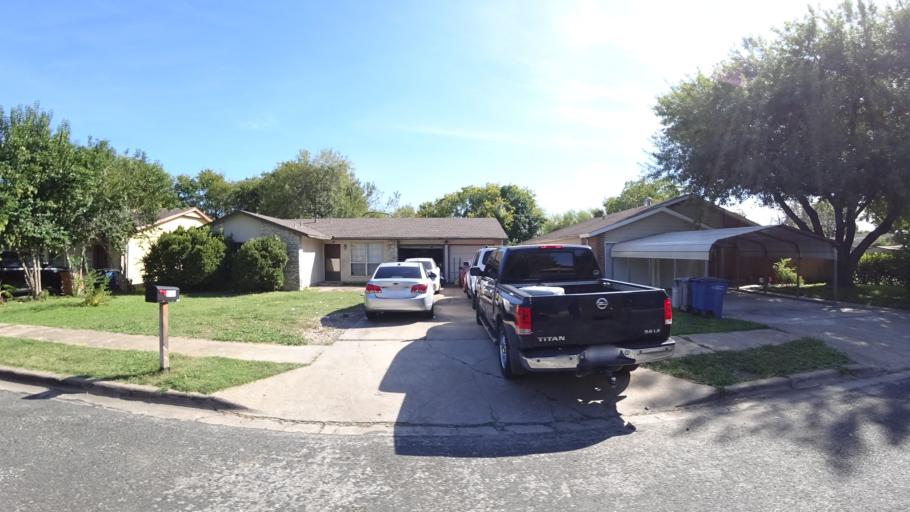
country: US
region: Texas
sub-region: Travis County
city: Onion Creek
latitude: 30.1944
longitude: -97.7523
